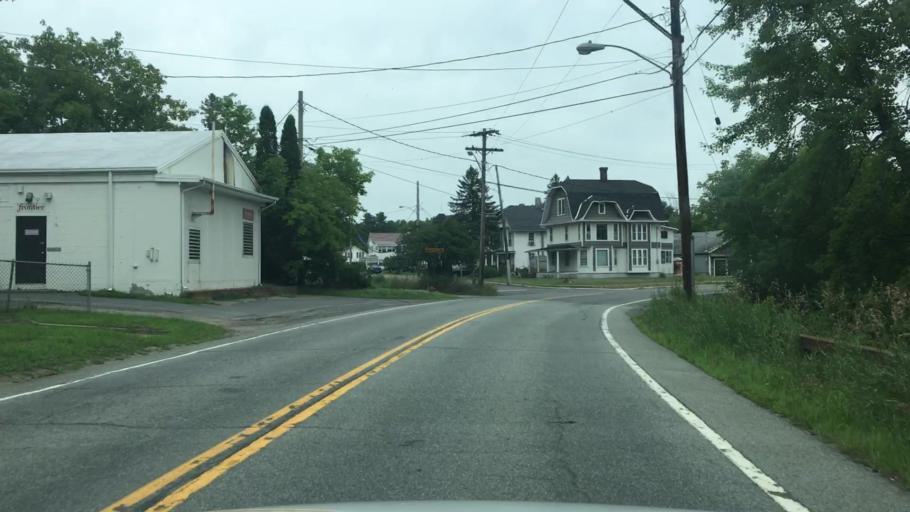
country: US
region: New York
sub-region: Clinton County
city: Peru
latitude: 44.4383
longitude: -73.6809
